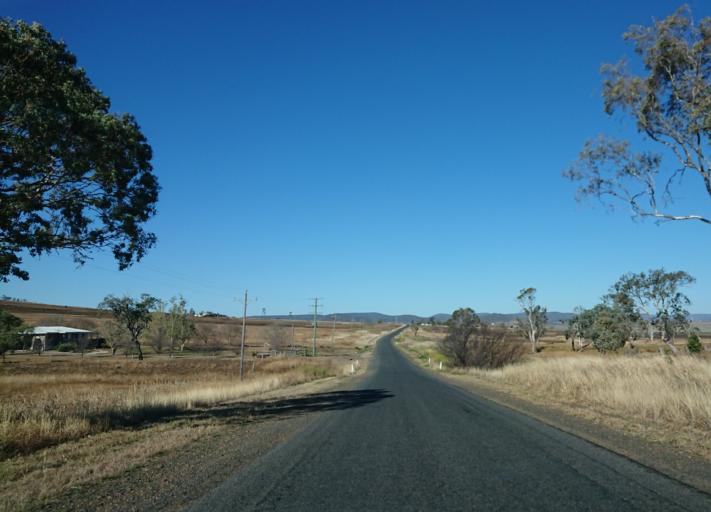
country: AU
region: Queensland
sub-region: Toowoomba
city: Top Camp
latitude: -27.8091
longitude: 151.9558
